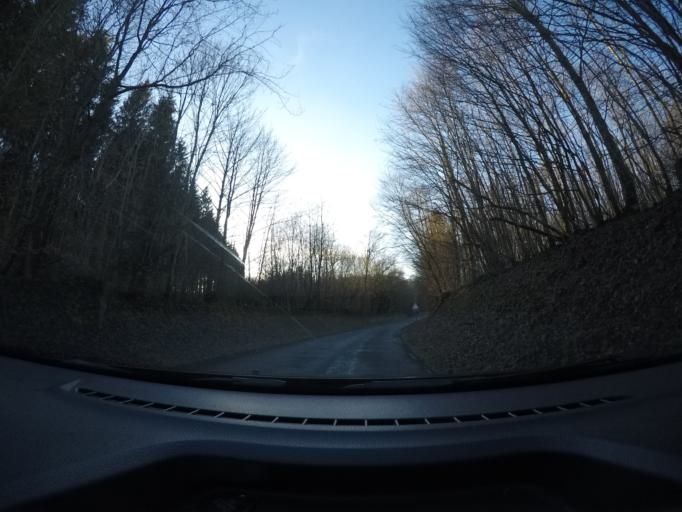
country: BE
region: Wallonia
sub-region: Province du Luxembourg
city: Tintigny
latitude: 49.6800
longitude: 5.5012
